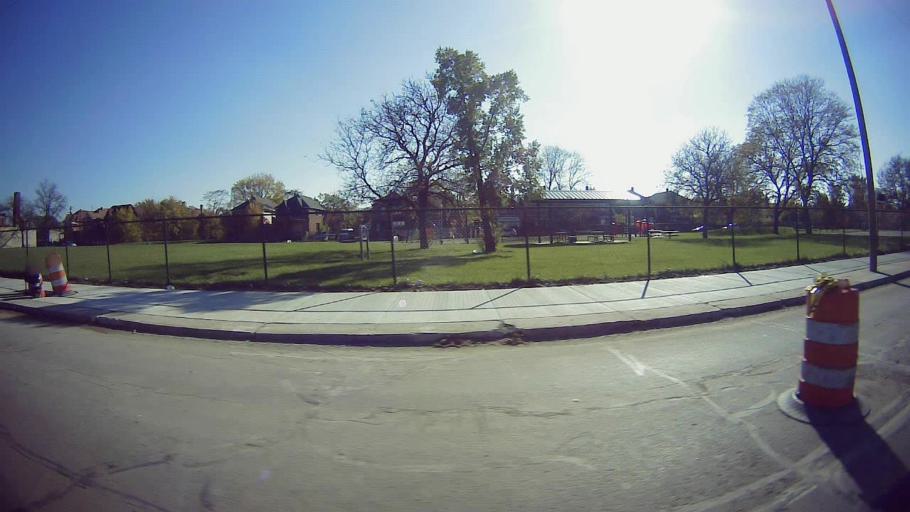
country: US
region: Michigan
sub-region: Wayne County
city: Highland Park
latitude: 42.3890
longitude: -83.1326
